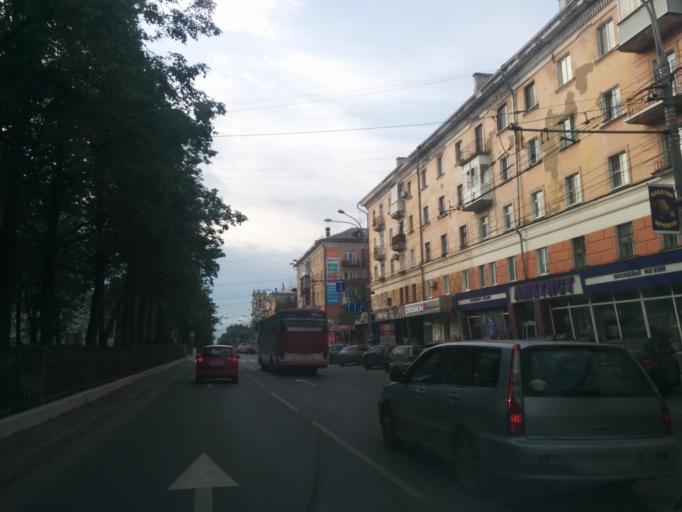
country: RU
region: Perm
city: Perm
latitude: 57.9992
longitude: 56.2505
